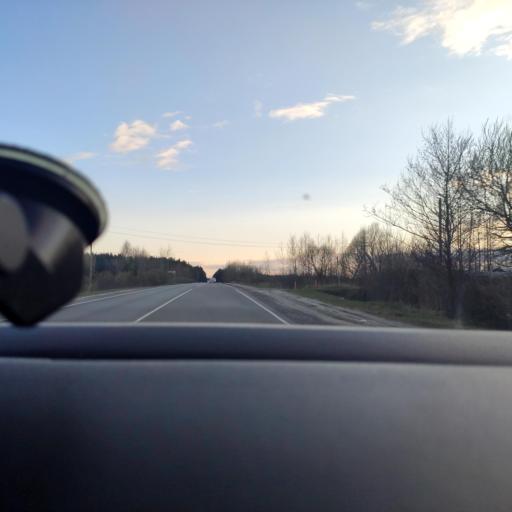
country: RU
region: Moskovskaya
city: Krasnyy Tkach
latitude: 55.4227
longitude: 39.1871
